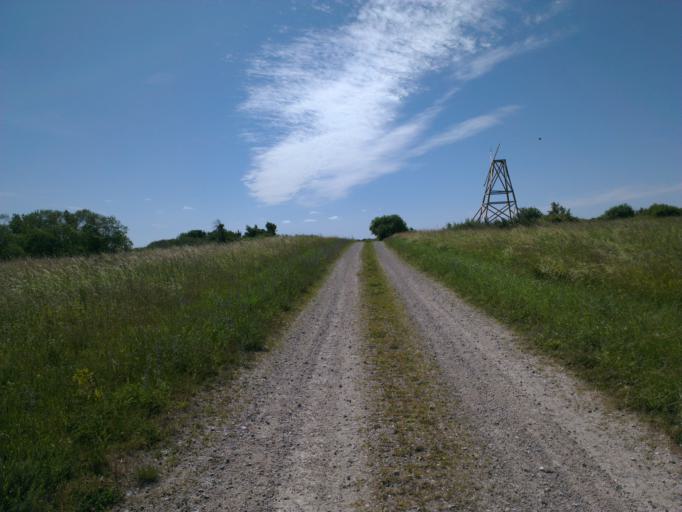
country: DK
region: Capital Region
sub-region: Frederikssund Kommune
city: Jaegerspris
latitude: 55.8788
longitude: 11.9386
